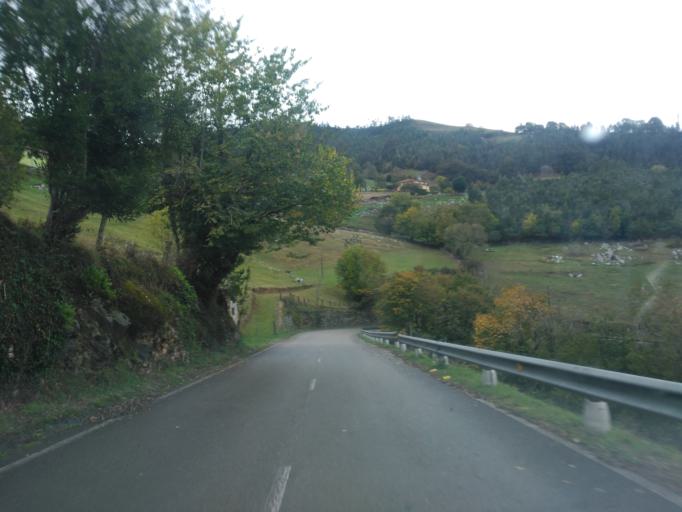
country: ES
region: Cantabria
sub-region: Provincia de Cantabria
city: Puente Viesgo
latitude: 43.2960
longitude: -3.9706
